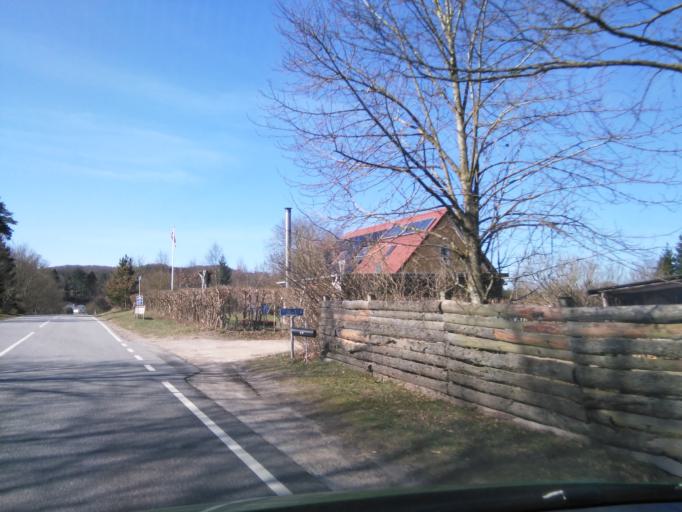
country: DK
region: Central Jutland
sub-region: Horsens Kommune
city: Braedstrup
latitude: 56.0141
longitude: 9.6822
